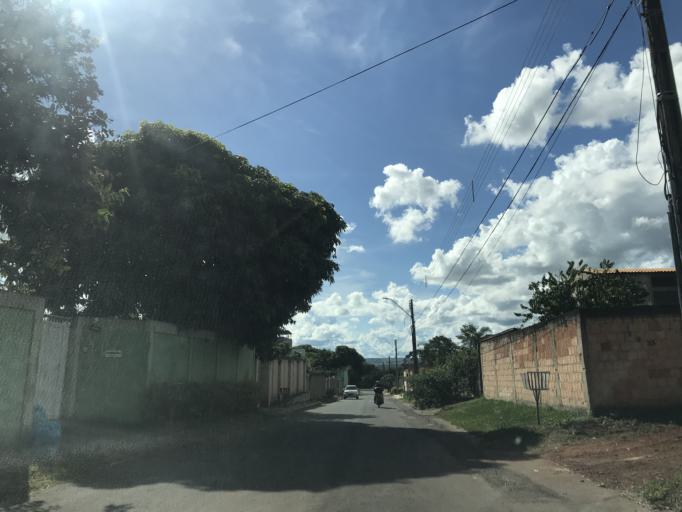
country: BR
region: Federal District
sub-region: Brasilia
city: Brasilia
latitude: -15.7374
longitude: -47.7503
